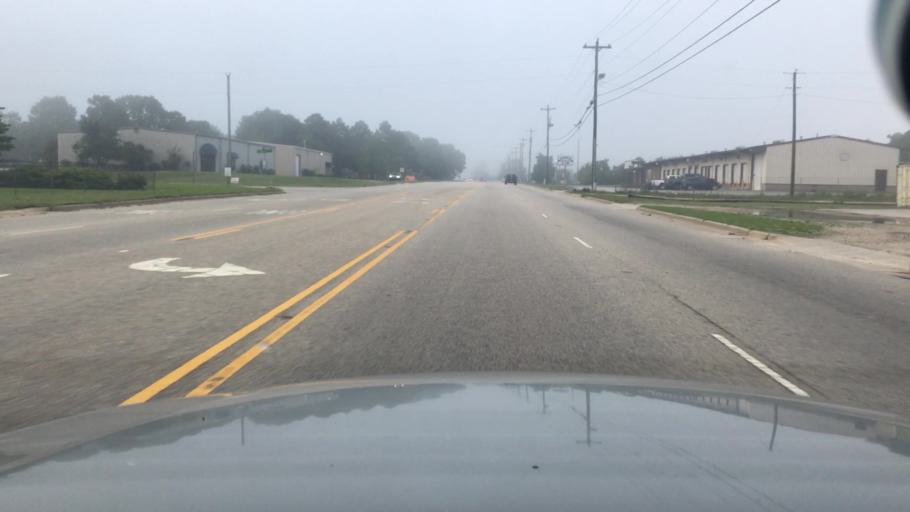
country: US
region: North Carolina
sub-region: Cumberland County
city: Hope Mills
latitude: 35.0171
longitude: -78.9187
